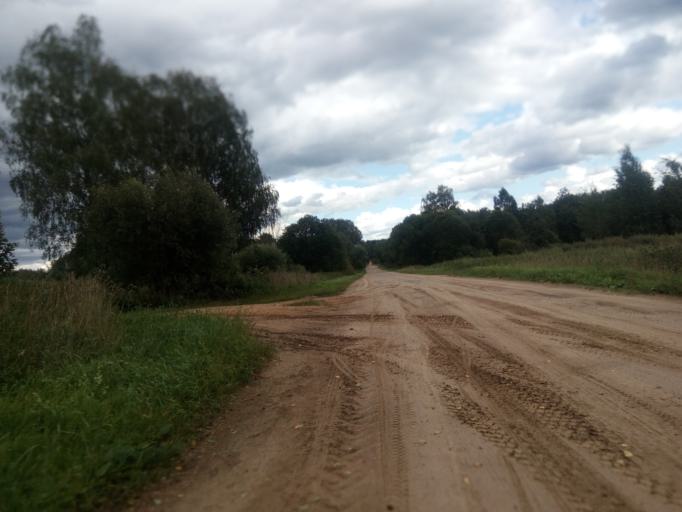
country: BY
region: Vitebsk
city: Dzisna
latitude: 55.7070
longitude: 28.3222
